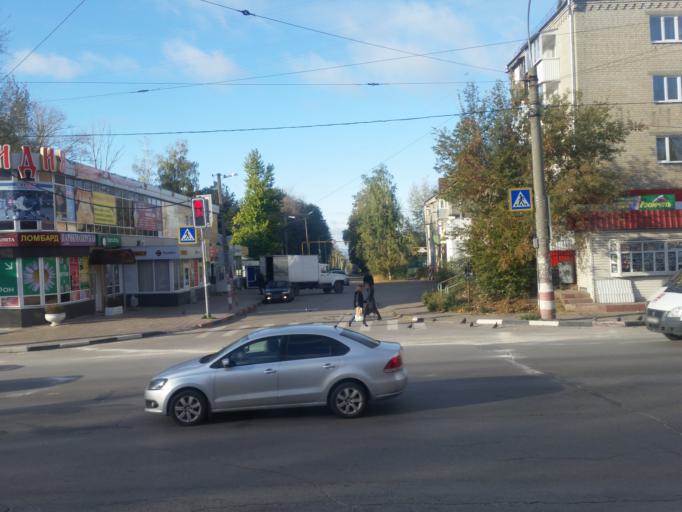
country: RU
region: Ulyanovsk
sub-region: Ulyanovskiy Rayon
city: Ulyanovsk
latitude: 54.3414
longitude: 48.3779
